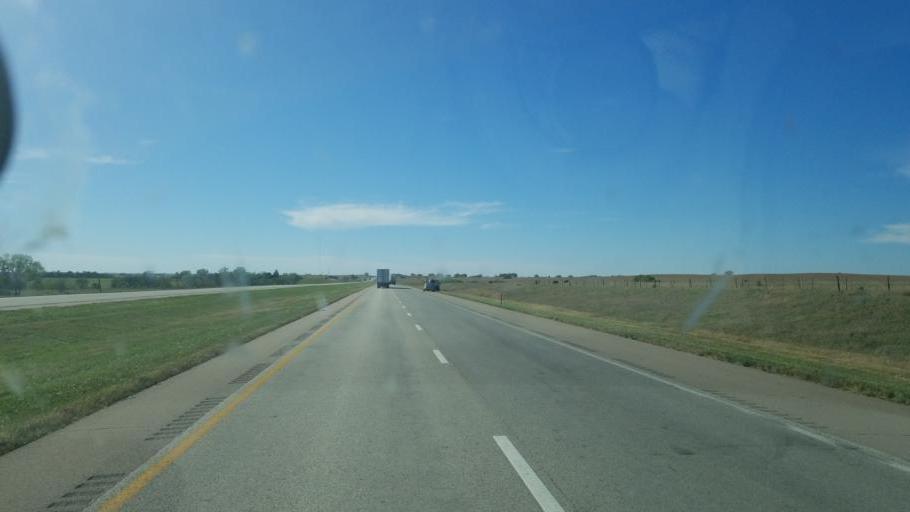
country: US
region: Kansas
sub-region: Saline County
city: Salina
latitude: 38.8784
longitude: -97.6953
